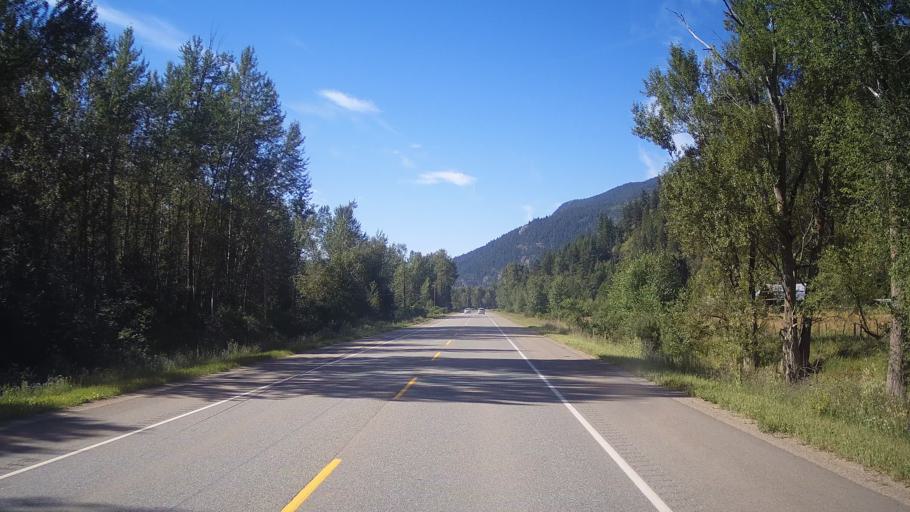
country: CA
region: British Columbia
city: Chase
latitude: 51.5010
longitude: -120.1763
